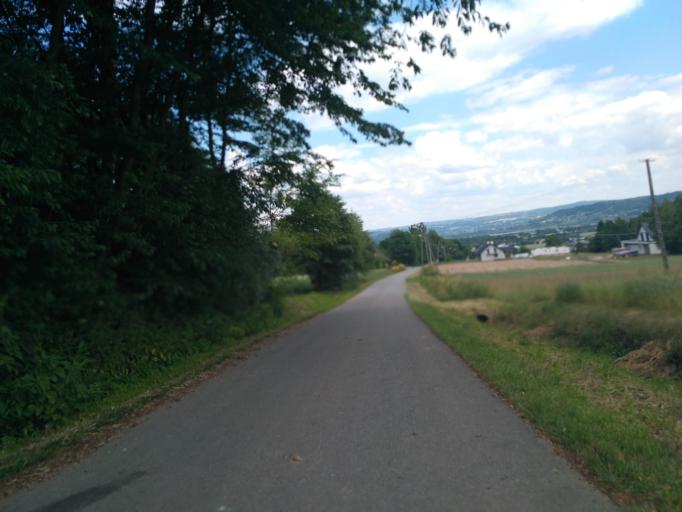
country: PL
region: Subcarpathian Voivodeship
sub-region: Powiat jasielski
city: Brzyska
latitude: 49.8069
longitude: 21.3850
